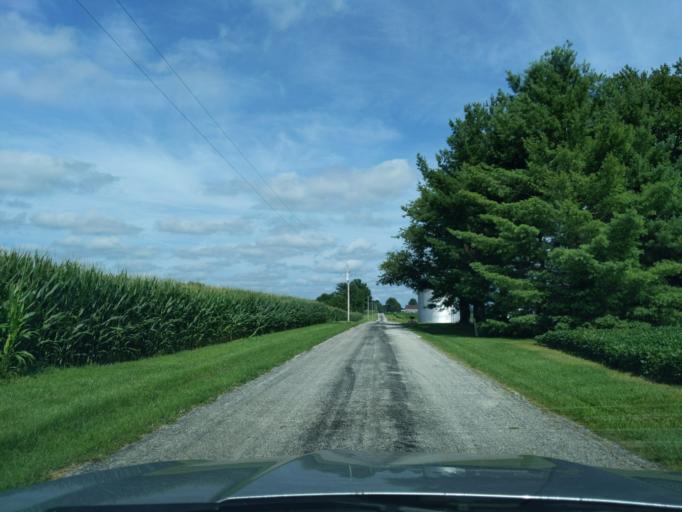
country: US
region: Indiana
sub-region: Decatur County
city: Greensburg
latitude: 39.2345
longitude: -85.4155
